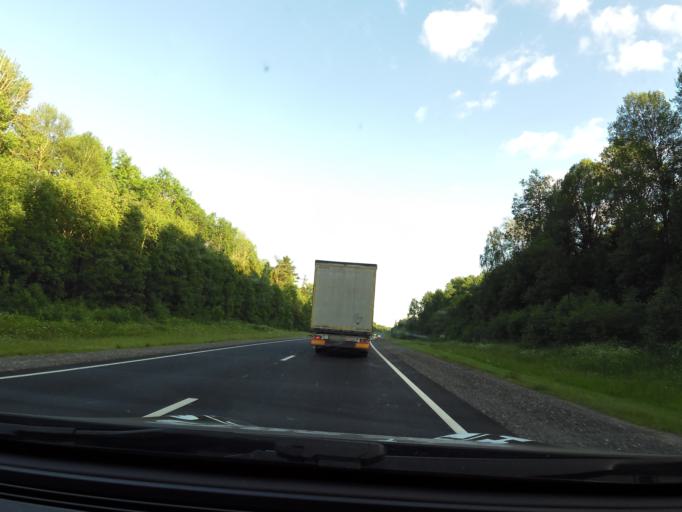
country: RU
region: Vologda
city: Gryazovets
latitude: 58.9450
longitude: 40.1734
